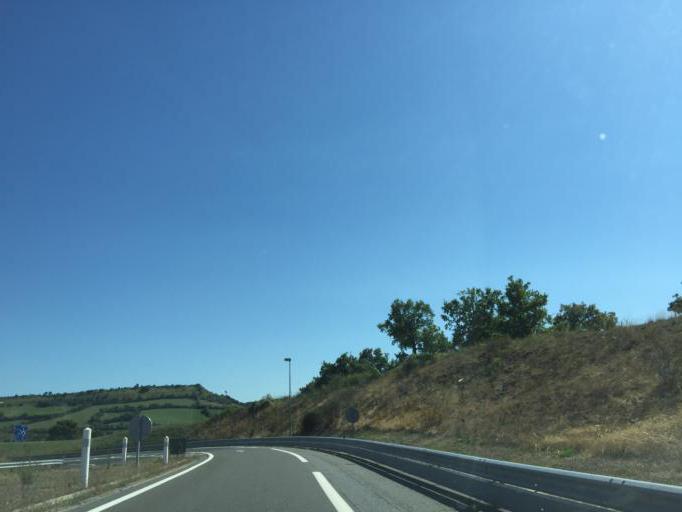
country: FR
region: Midi-Pyrenees
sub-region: Departement de l'Aveyron
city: Severac-le-Chateau
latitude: 44.3323
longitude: 3.0768
